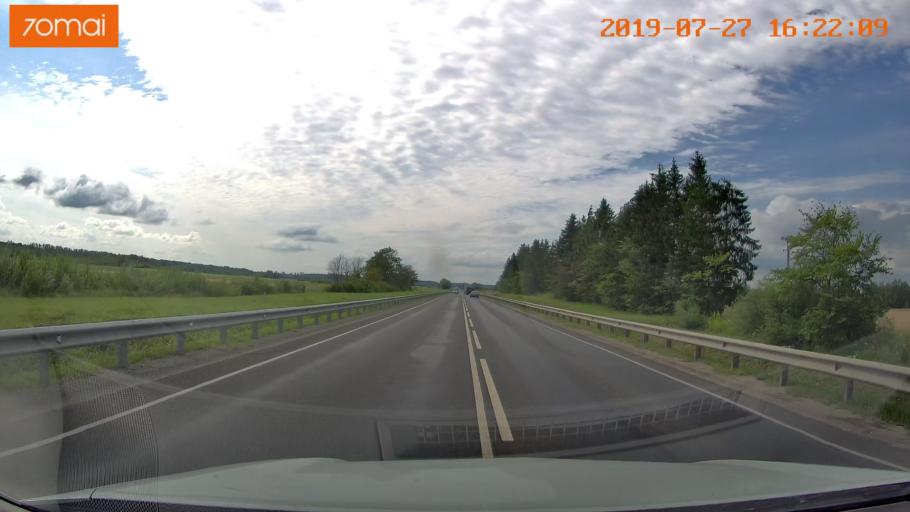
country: RU
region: Kaliningrad
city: Chernyakhovsk
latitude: 54.6268
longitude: 21.5017
